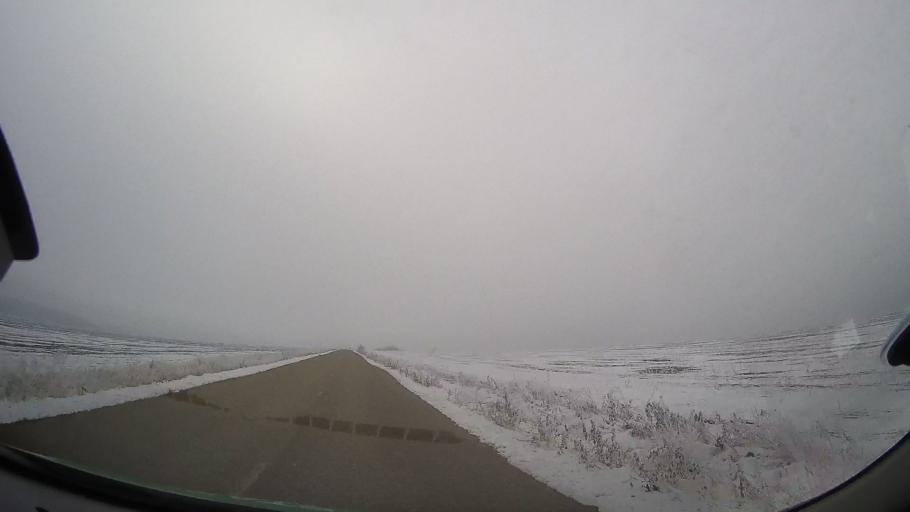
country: RO
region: Vaslui
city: Coroiesti
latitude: 46.2357
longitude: 27.4777
